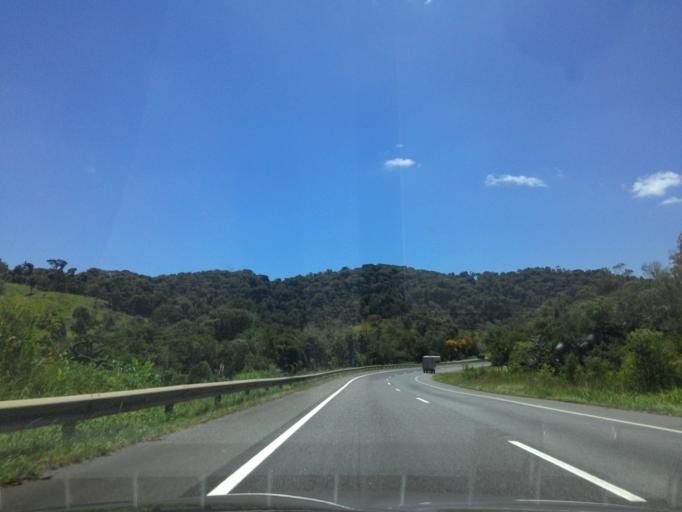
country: BR
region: Parana
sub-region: Antonina
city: Antonina
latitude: -25.0364
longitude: -48.5363
